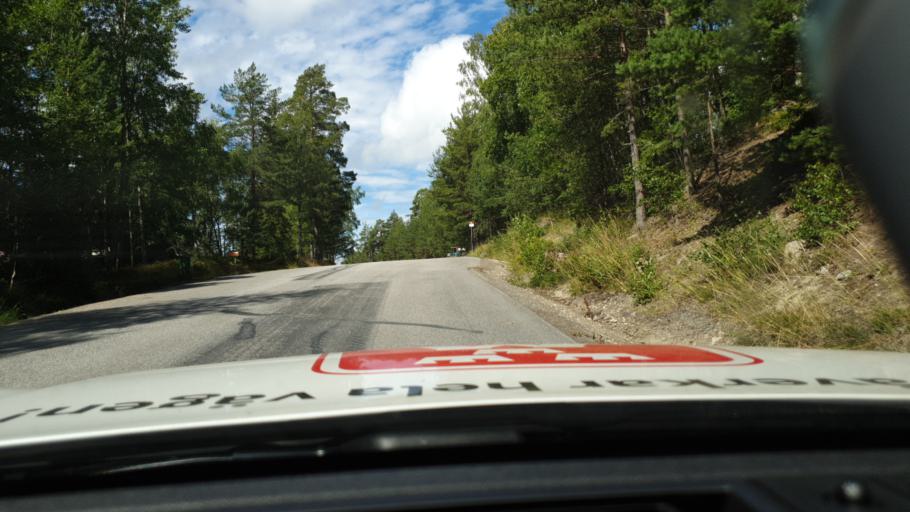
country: SE
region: Stockholm
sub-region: Haninge Kommun
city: Jordbro
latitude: 59.0251
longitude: 18.1566
